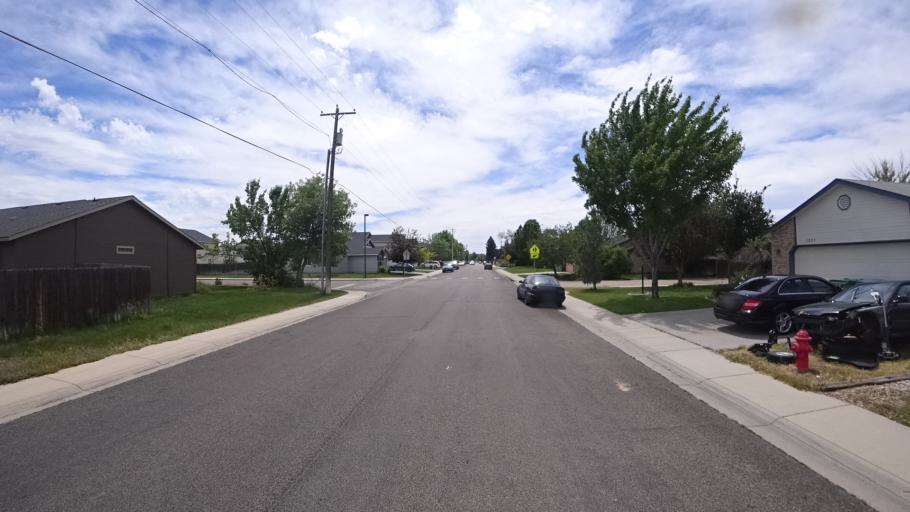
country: US
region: Idaho
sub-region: Ada County
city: Garden City
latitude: 43.6162
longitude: -116.3092
